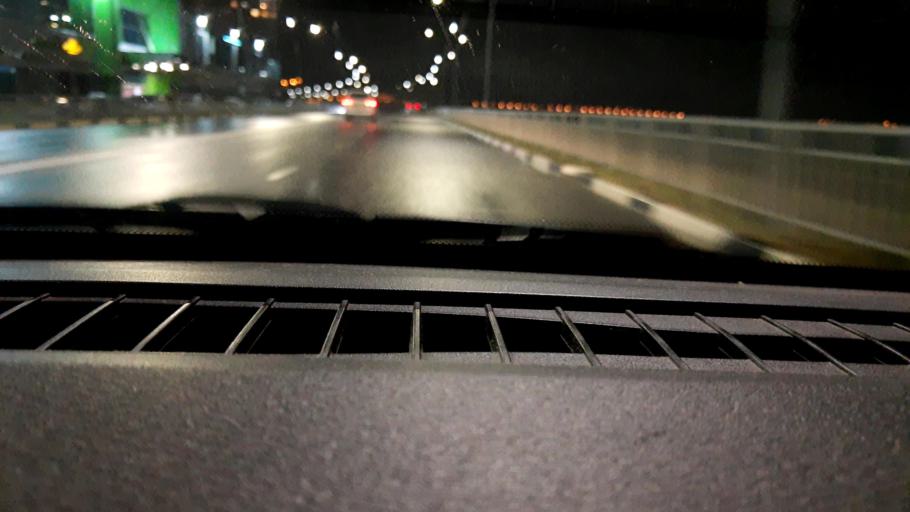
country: RU
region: Nizjnij Novgorod
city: Nizhniy Novgorod
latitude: 56.3410
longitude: 43.9592
